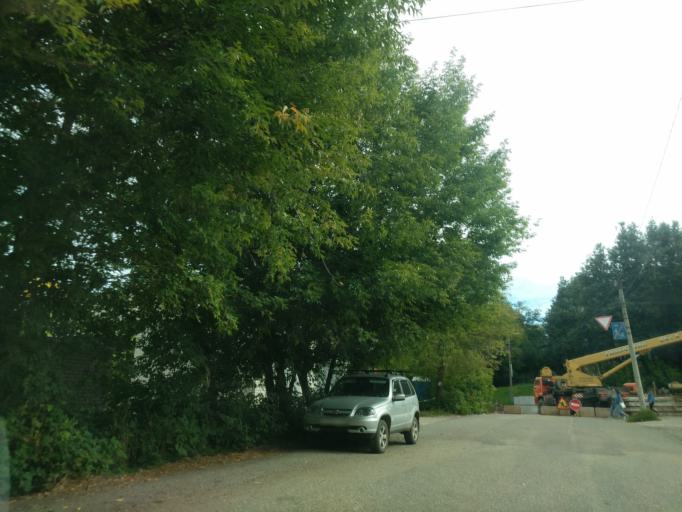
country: RU
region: Kirov
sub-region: Kirovo-Chepetskiy Rayon
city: Kirov
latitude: 58.5978
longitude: 49.6495
